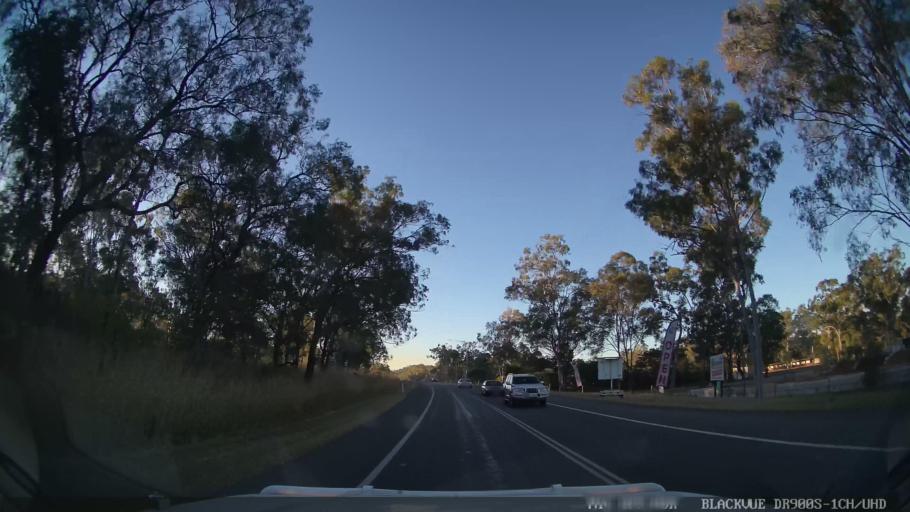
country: AU
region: Queensland
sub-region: Gladstone
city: Toolooa
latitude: -23.9563
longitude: 151.2200
